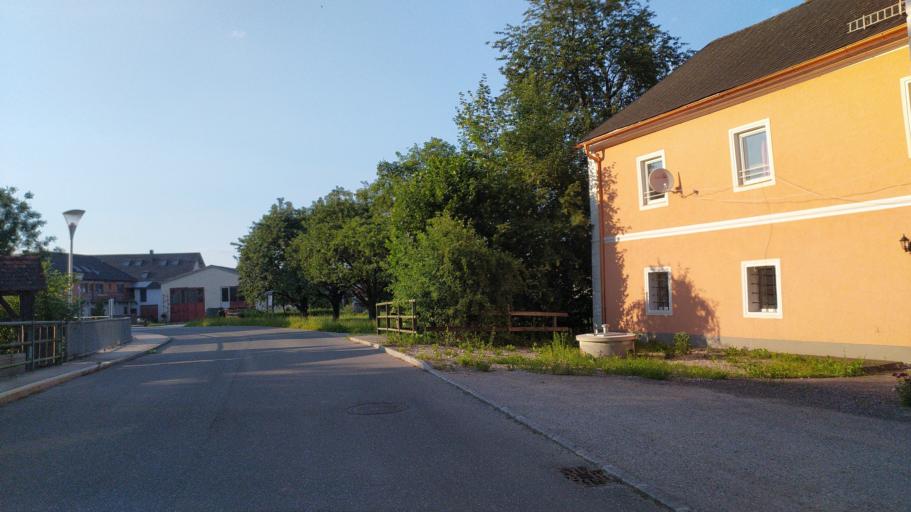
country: AT
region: Lower Austria
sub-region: Politischer Bezirk Amstetten
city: Ennsdorf
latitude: 48.2099
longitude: 14.5692
